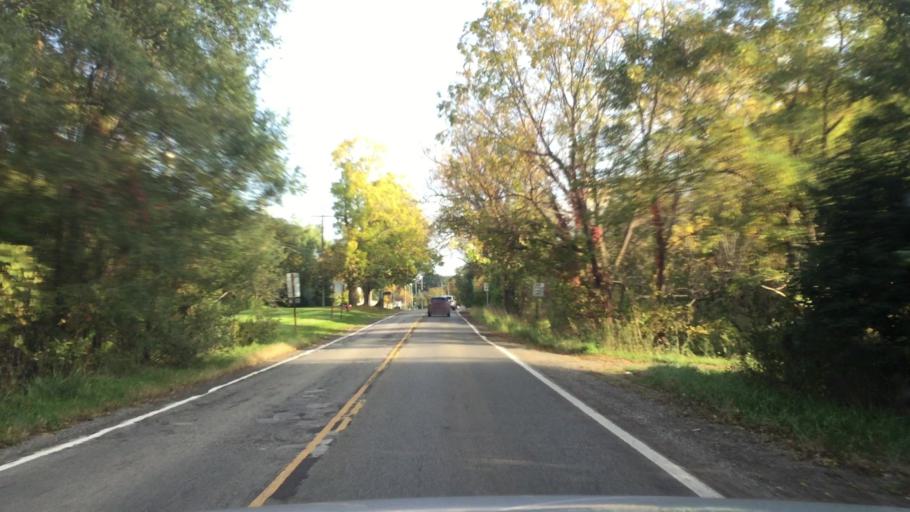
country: US
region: Michigan
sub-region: Oakland County
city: Wolverine Lake
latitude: 42.6279
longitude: -83.4602
